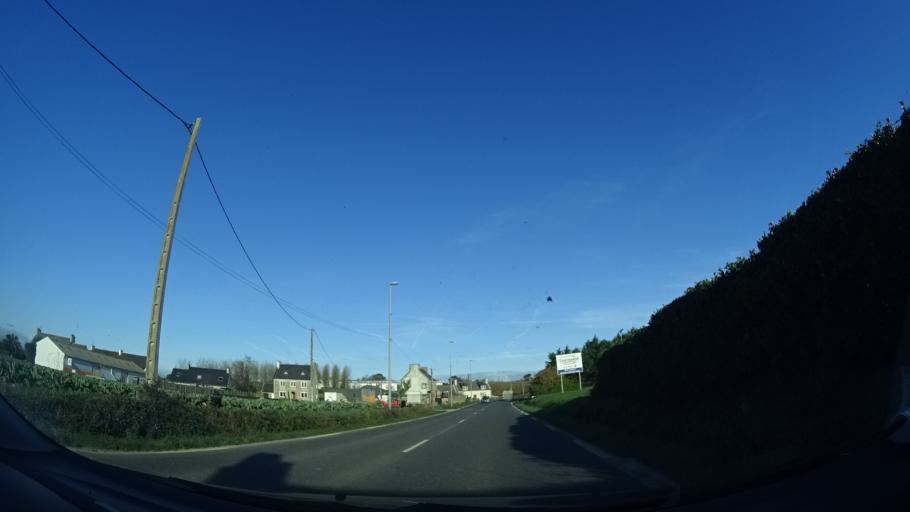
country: FR
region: Brittany
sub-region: Departement du Finistere
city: Saint-Pol-de-Leon
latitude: 48.6806
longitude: -4.0037
